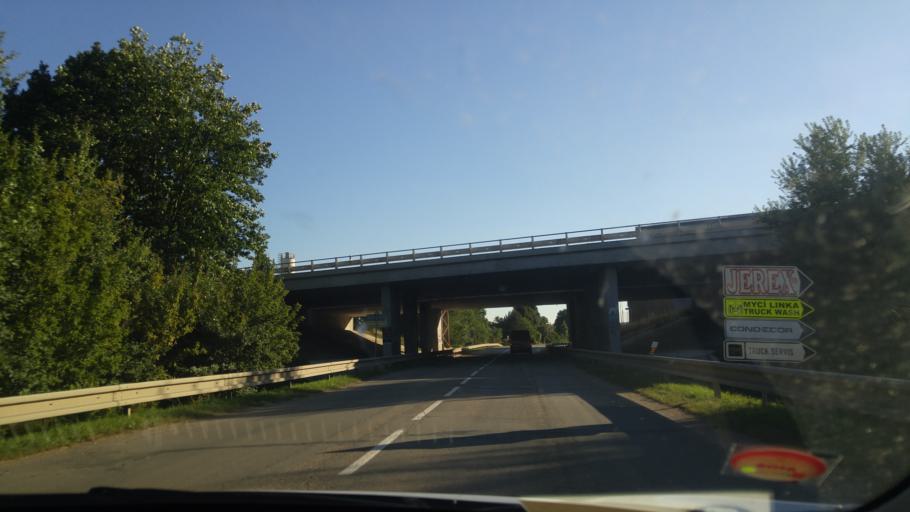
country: CZ
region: South Moravian
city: Ricany
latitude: 49.2166
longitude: 16.4110
